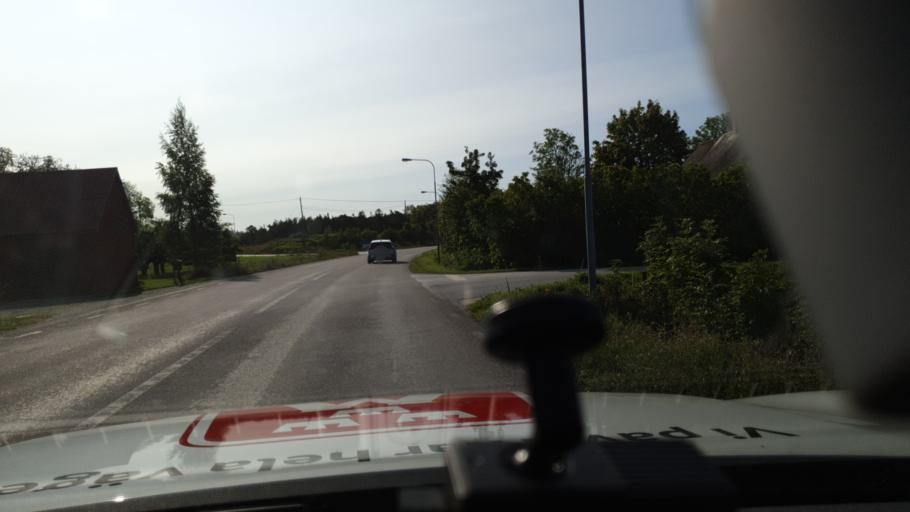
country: SE
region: Gotland
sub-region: Gotland
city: Klintehamn
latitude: 57.3312
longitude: 18.1925
